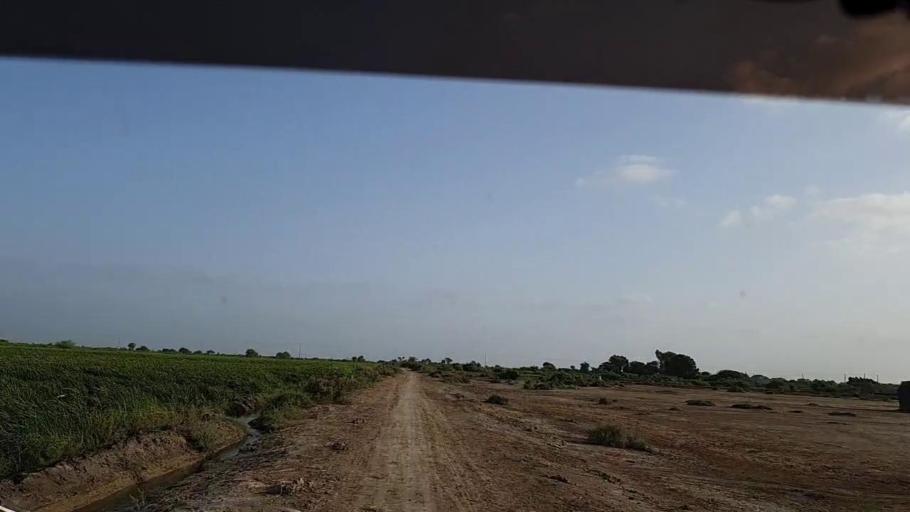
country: PK
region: Sindh
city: Badin
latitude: 24.5557
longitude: 68.8631
